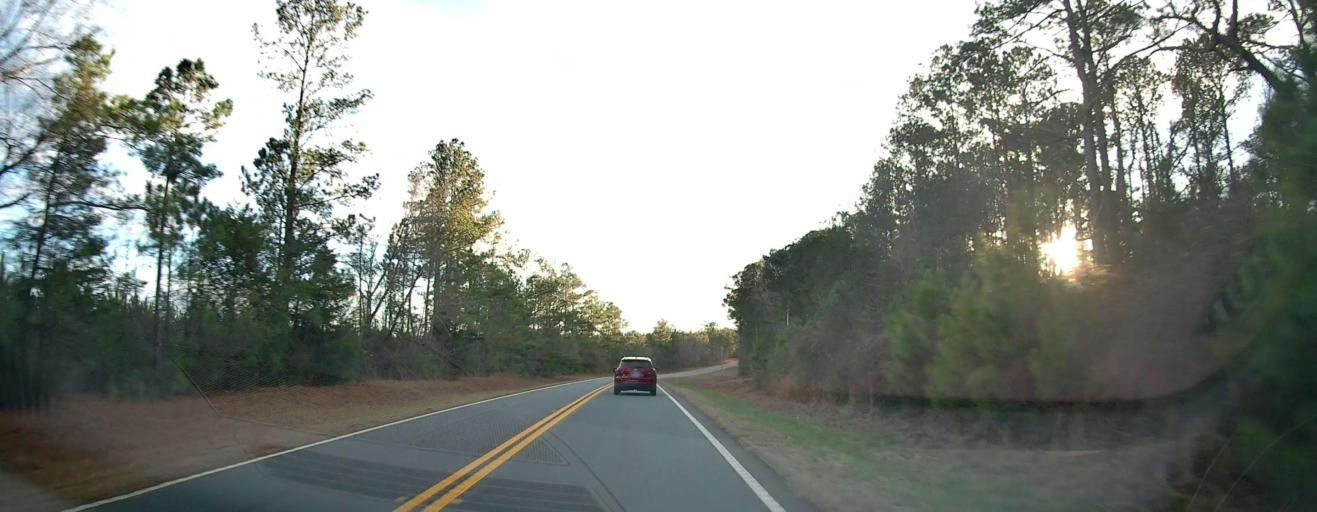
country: US
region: Georgia
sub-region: Talbot County
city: Sardis
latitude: 32.7305
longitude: -84.6216
